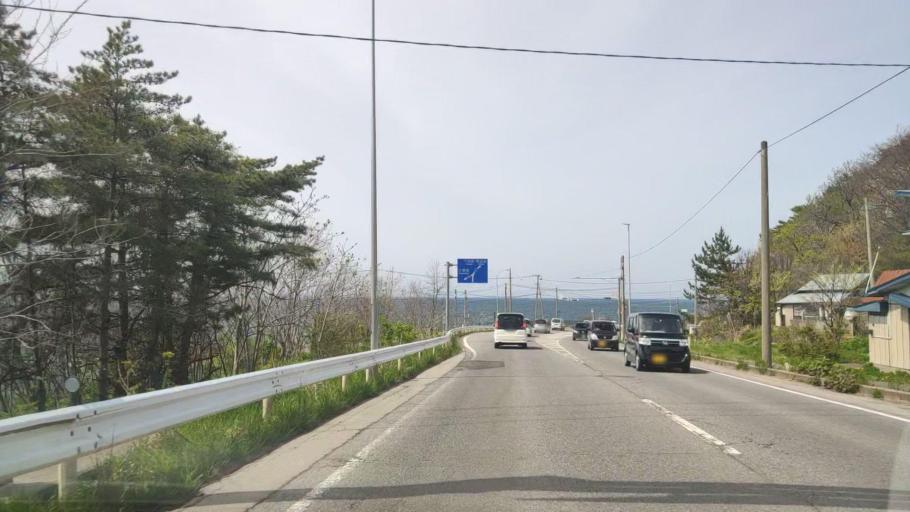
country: JP
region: Aomori
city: Aomori Shi
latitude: 40.8766
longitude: 140.8506
